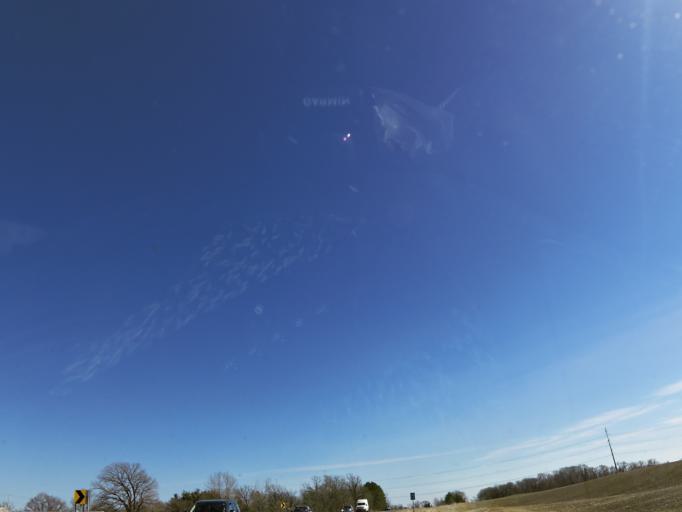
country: US
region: Minnesota
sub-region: Wright County
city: Rockford
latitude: 45.1148
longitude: -93.7900
